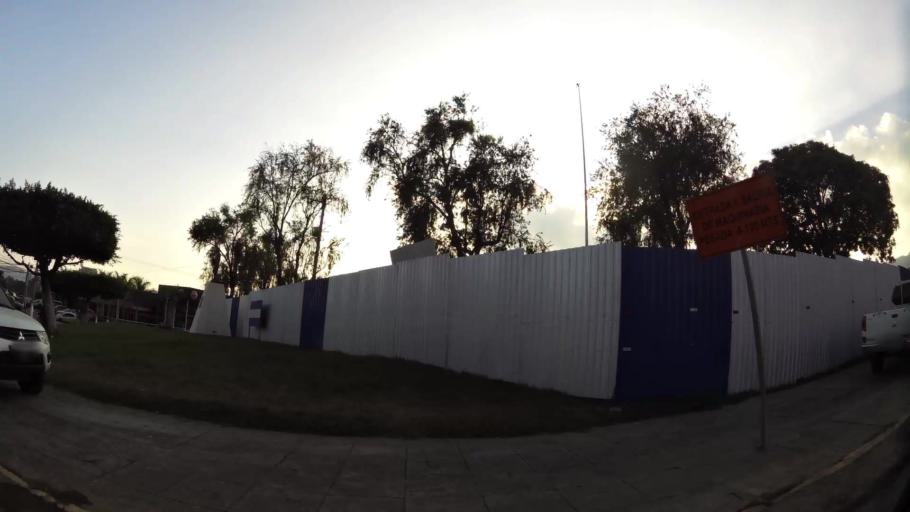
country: SV
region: La Libertad
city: Antiguo Cuscatlan
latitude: 13.7038
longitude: -89.2487
